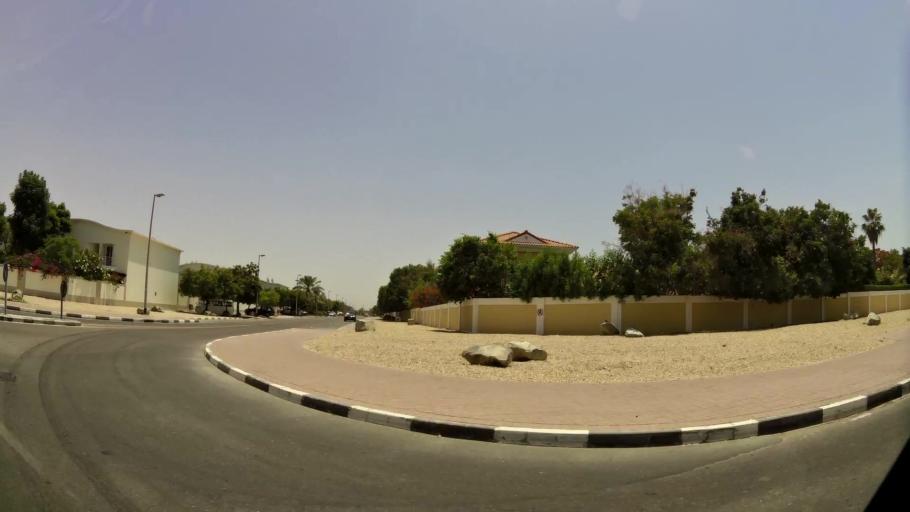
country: AE
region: Dubai
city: Dubai
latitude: 25.2008
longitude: 55.2450
